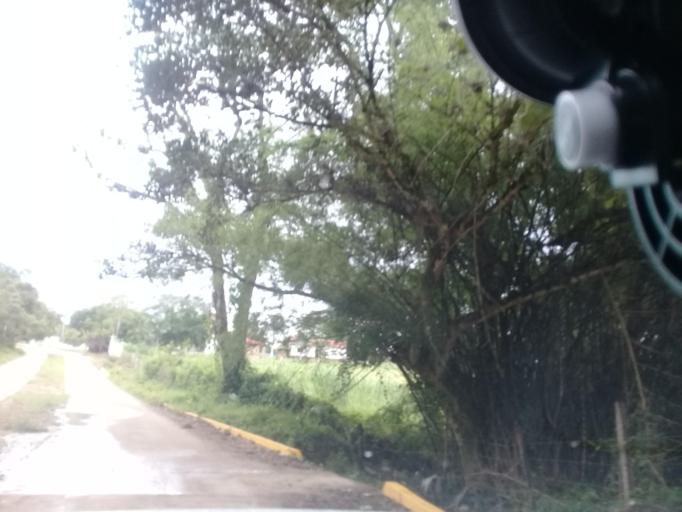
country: MX
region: Hidalgo
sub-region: Huejutla de Reyes
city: Chalahuiyapa
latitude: 21.1620
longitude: -98.3545
